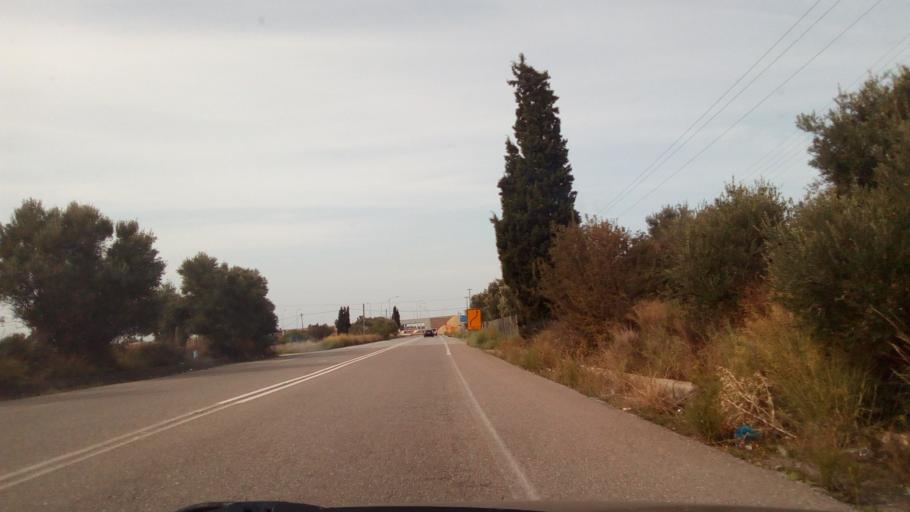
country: GR
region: West Greece
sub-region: Nomos Aitolias kai Akarnanias
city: Antirrio
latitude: 38.3416
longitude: 21.7656
